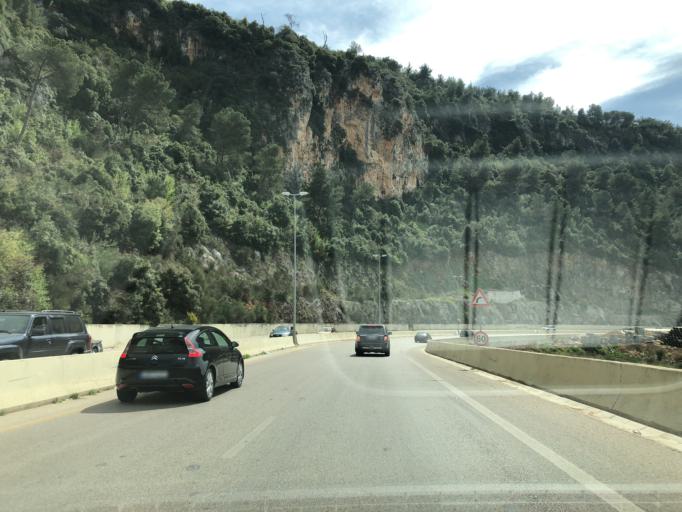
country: LB
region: Mont-Liban
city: Jdaidet el Matn
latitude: 33.8996
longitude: 35.6403
